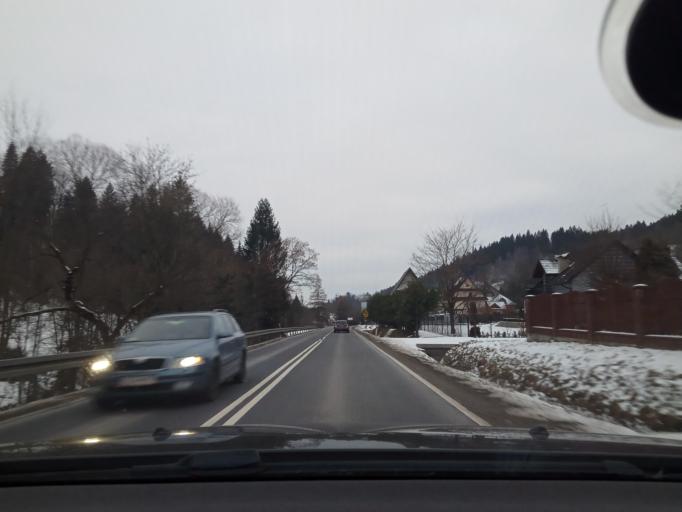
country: PL
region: Lesser Poland Voivodeship
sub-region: Powiat limanowski
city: Lubomierz
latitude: 49.6171
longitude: 20.1761
